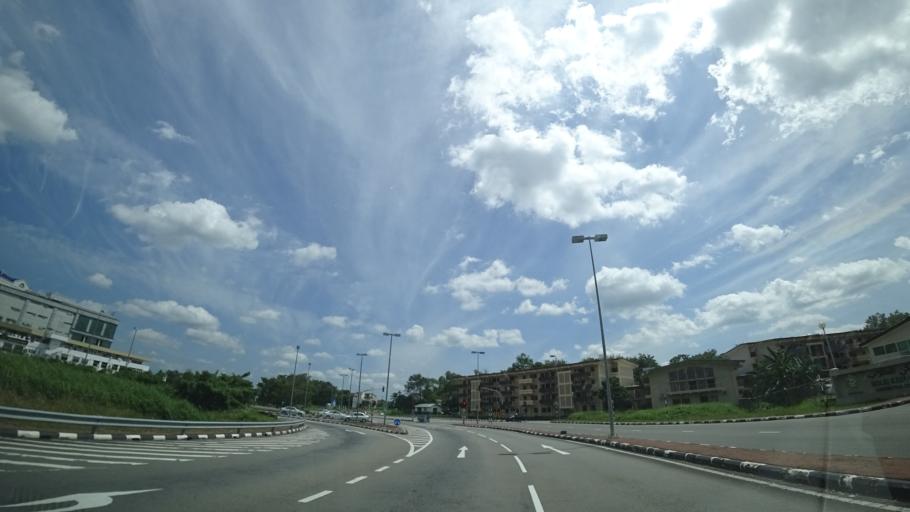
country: BN
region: Brunei and Muara
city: Bandar Seri Begawan
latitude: 4.9059
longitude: 114.9147
